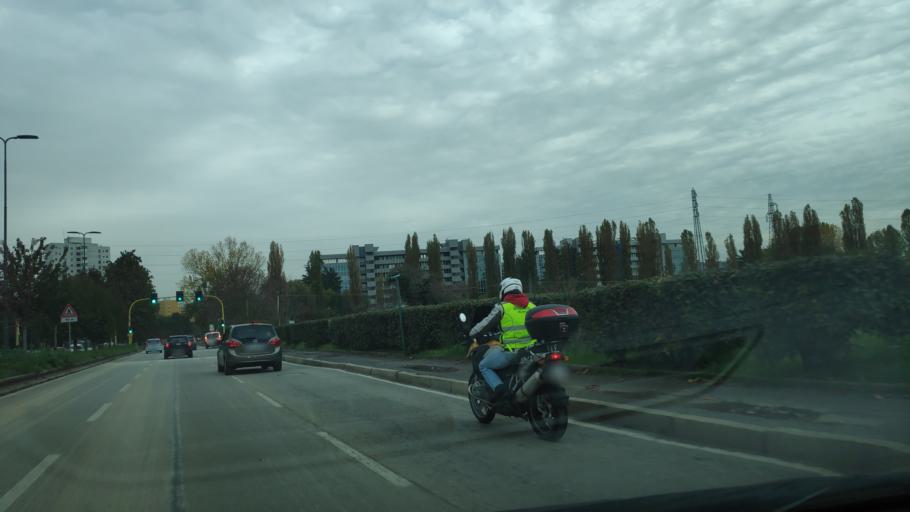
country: IT
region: Lombardy
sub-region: Citta metropolitana di Milano
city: Rozzano
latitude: 45.4059
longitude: 9.1753
